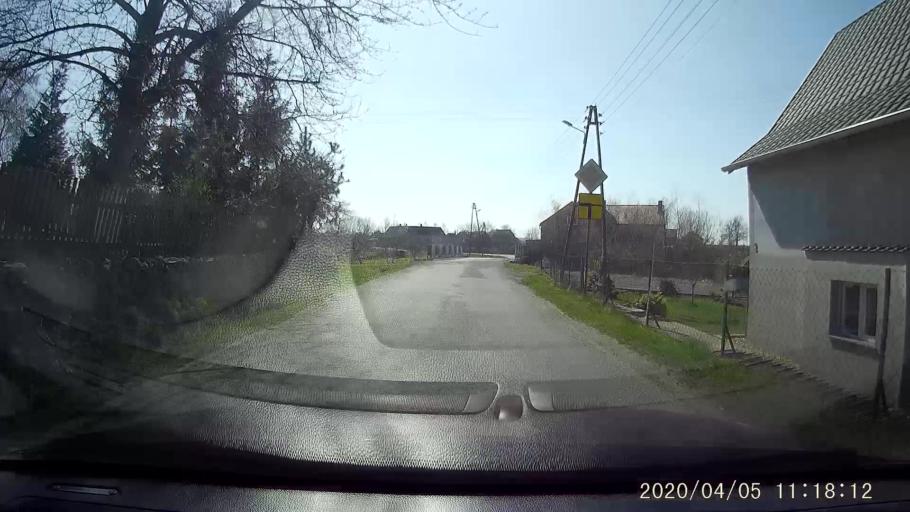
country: PL
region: Lower Silesian Voivodeship
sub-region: Powiat zgorzelecki
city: Sulikow
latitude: 51.0651
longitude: 15.1062
